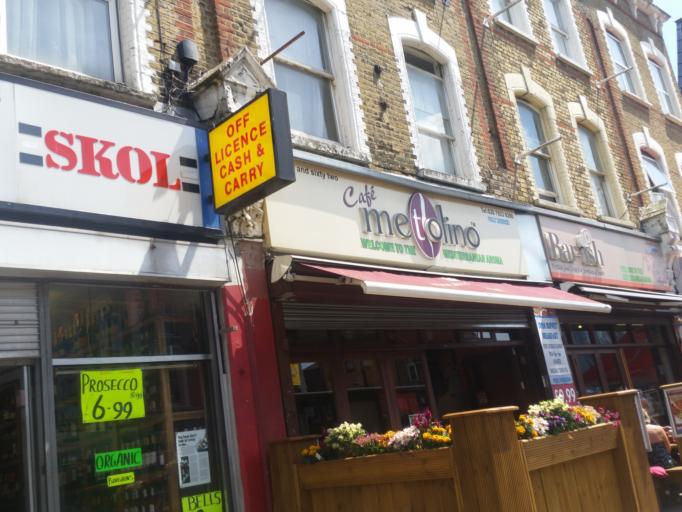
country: GB
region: England
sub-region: Greater London
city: Hackney
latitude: 51.5562
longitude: -0.0746
